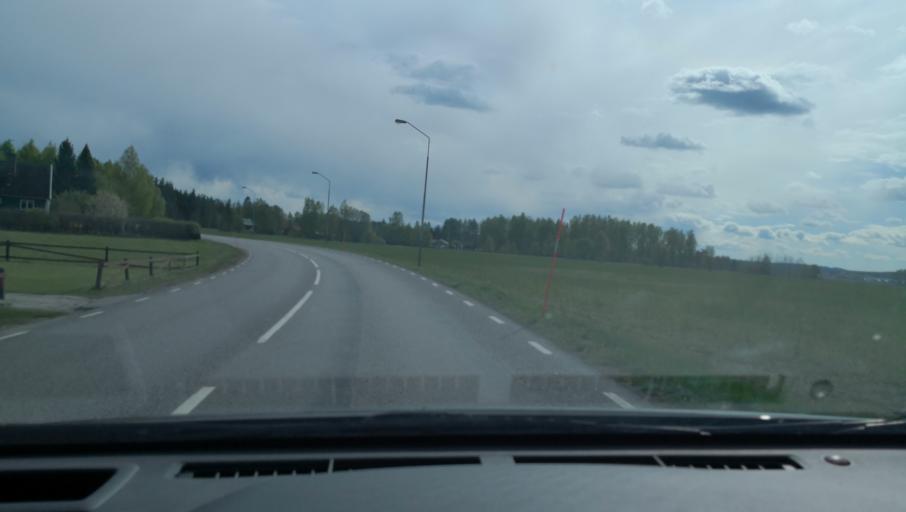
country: SE
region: OErebro
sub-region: Kumla Kommun
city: Kumla
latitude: 59.0859
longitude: 15.1582
